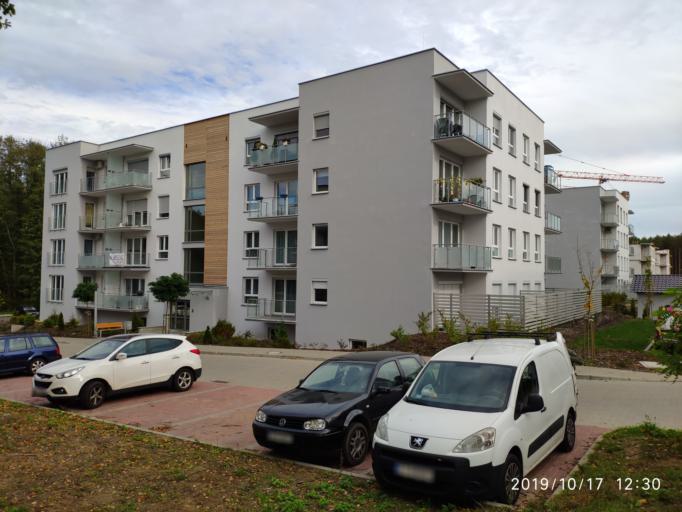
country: PL
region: Lubusz
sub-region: Zielona Gora
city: Zielona Gora
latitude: 51.9386
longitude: 15.5657
